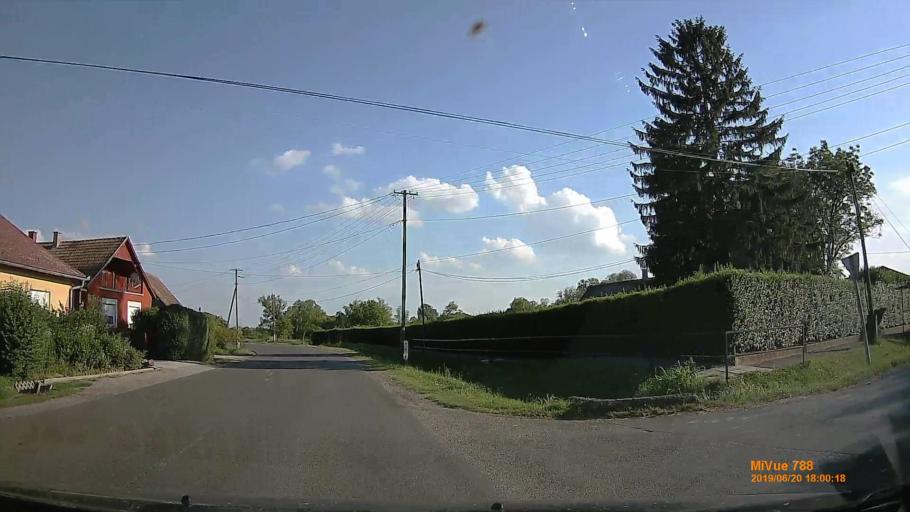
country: HU
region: Baranya
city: Buekkoesd
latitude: 46.0899
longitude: 17.9811
